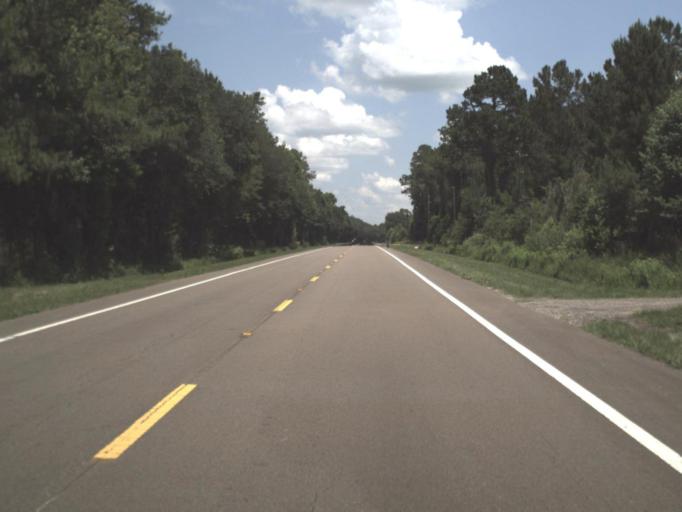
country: US
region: Florida
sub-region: Alachua County
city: Alachua
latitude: 29.7831
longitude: -82.3758
